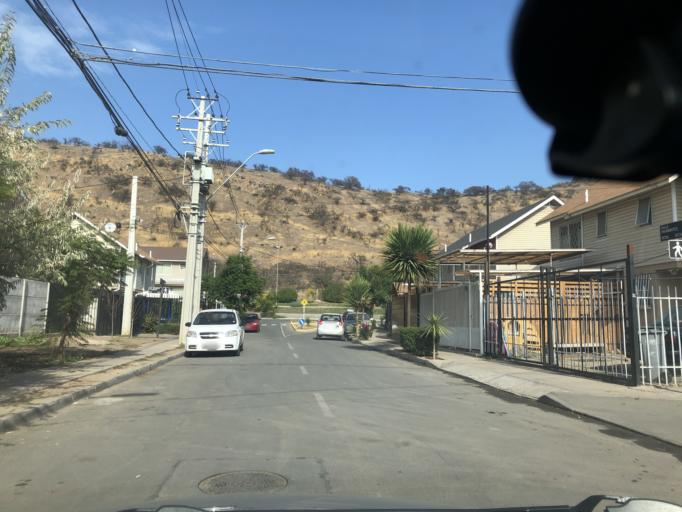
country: CL
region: Santiago Metropolitan
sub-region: Provincia de Cordillera
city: Puente Alto
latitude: -33.6008
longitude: -70.5504
